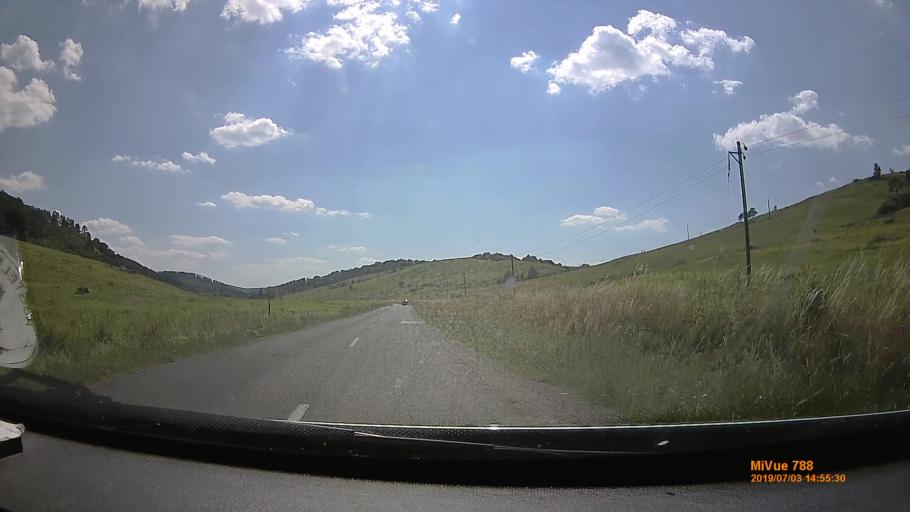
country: HU
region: Borsod-Abauj-Zemplen
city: Putnok
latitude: 48.2630
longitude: 20.4026
